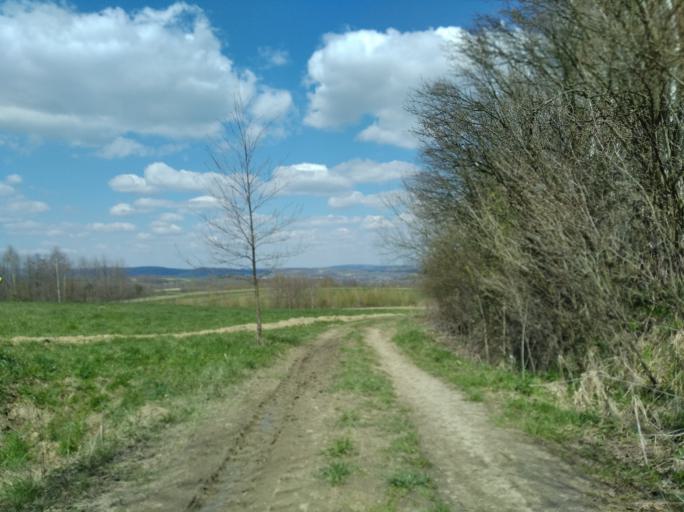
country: PL
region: Subcarpathian Voivodeship
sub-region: Powiat strzyzowski
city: Wysoka Strzyzowska
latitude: 49.8371
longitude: 21.7658
